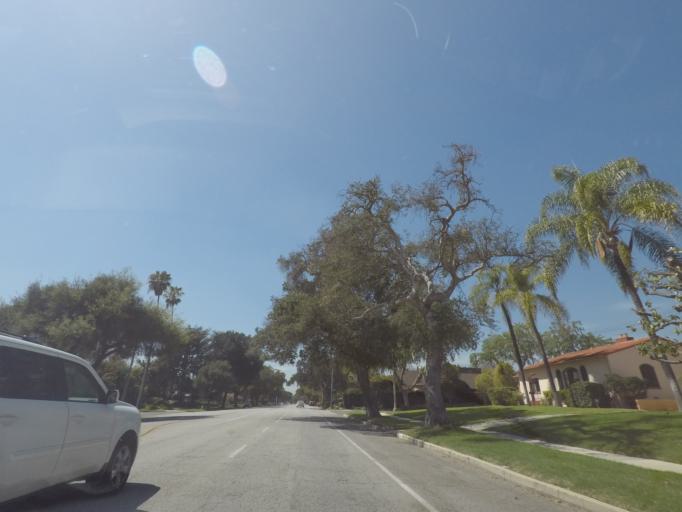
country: US
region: California
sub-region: Los Angeles County
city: East Pasadena
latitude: 34.1583
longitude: -118.1025
